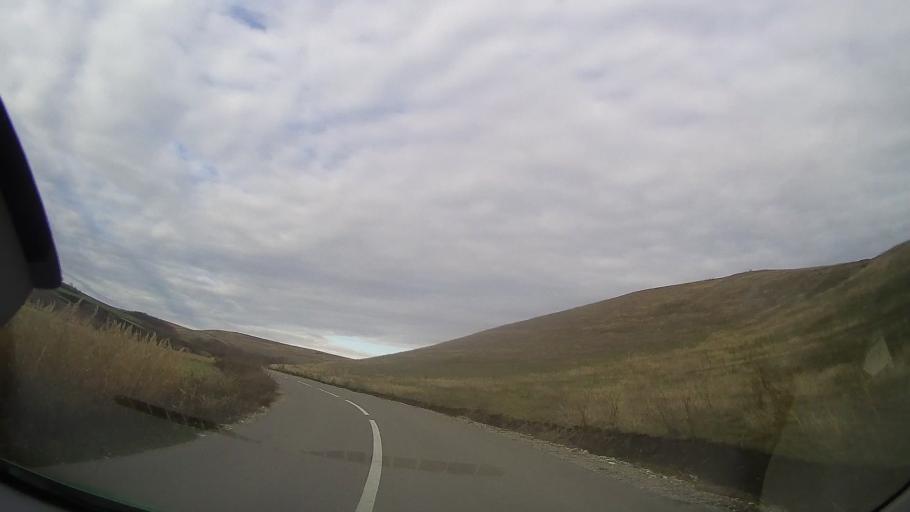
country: RO
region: Bistrita-Nasaud
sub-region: Comuna Silvasu de Campie
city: Silvasu de Campie
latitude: 46.8045
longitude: 24.2990
